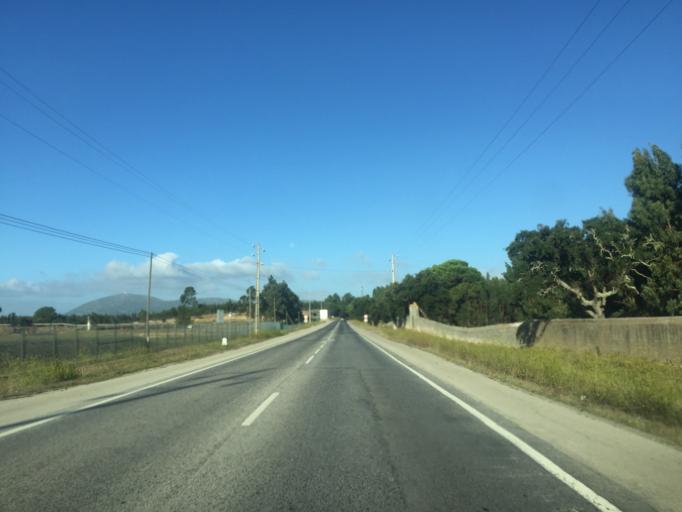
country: PT
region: Lisbon
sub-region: Azambuja
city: Aveiras de Cima
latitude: 39.1723
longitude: -8.9294
